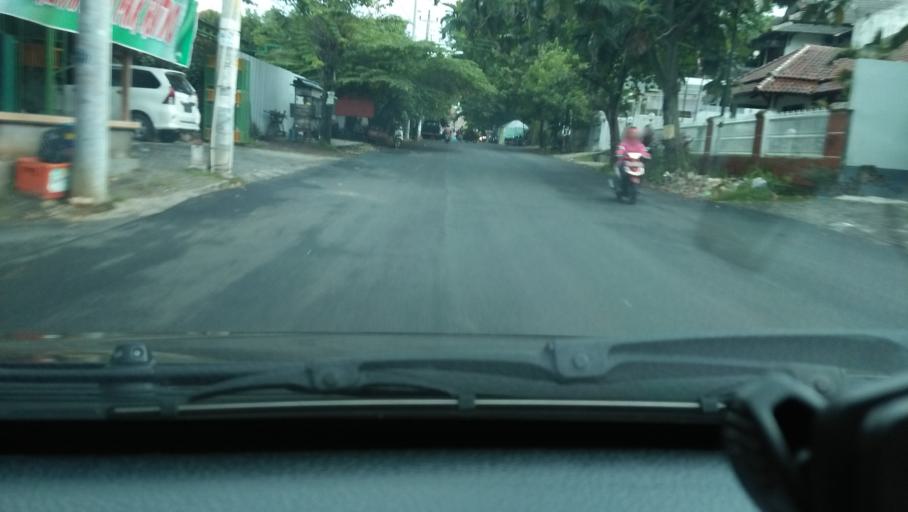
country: ID
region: Central Java
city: Semarang
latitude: -7.0640
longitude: 110.4168
